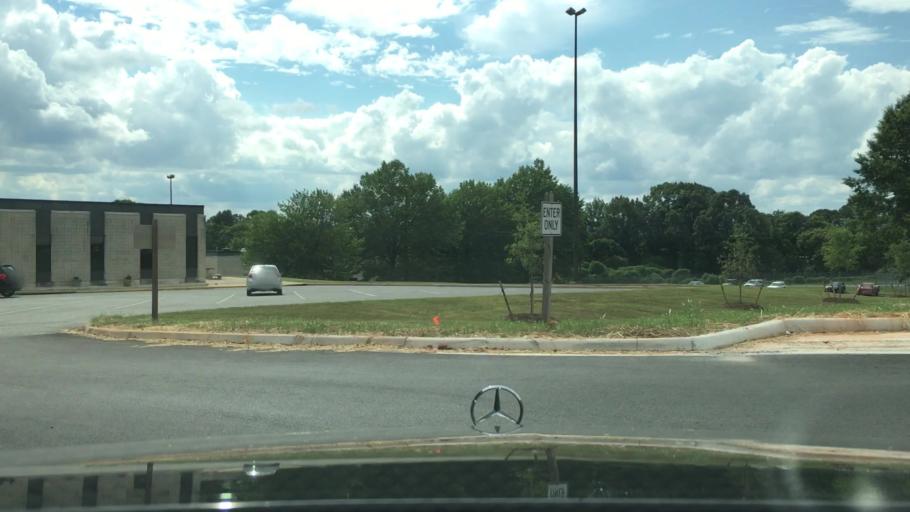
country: US
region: Virginia
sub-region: City of Lynchburg
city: West Lynchburg
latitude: 37.3812
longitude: -79.1606
